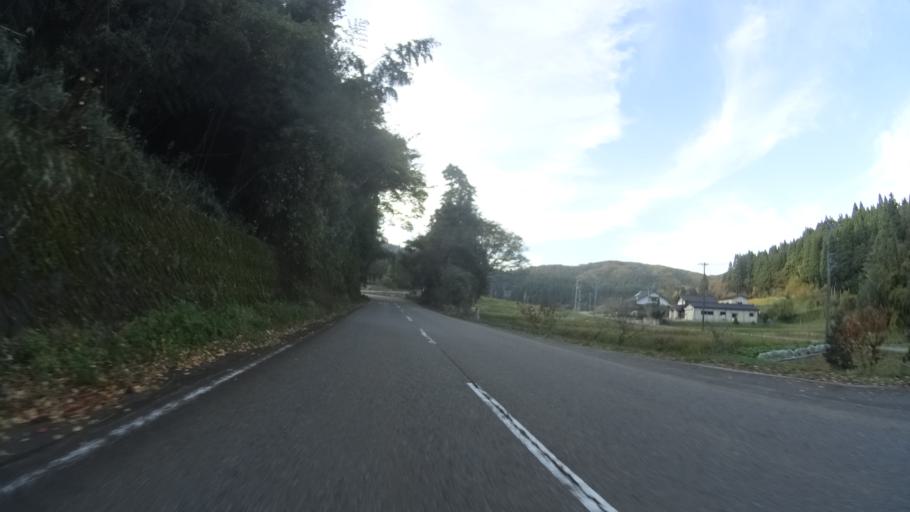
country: JP
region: Ishikawa
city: Nanao
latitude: 37.1941
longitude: 136.7159
